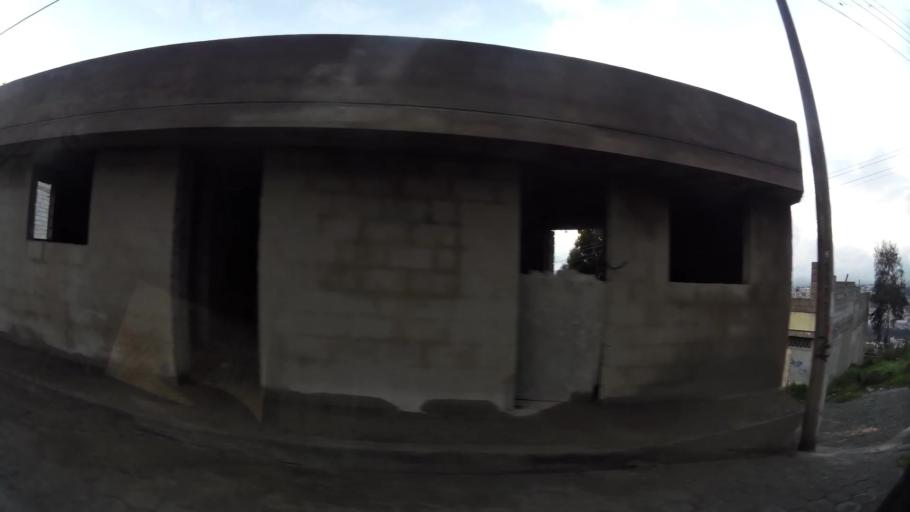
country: EC
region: Pichincha
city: Quito
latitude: -0.0944
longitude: -78.5113
